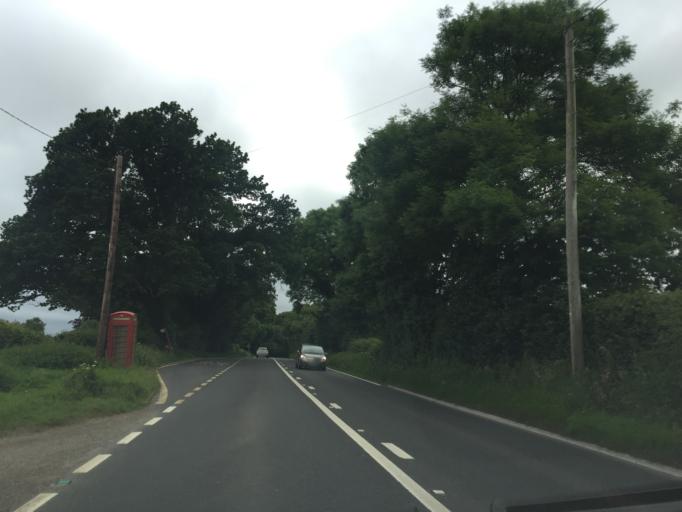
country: GB
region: England
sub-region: Dorset
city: Lytchett Matravers
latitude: 50.7753
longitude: -2.1446
